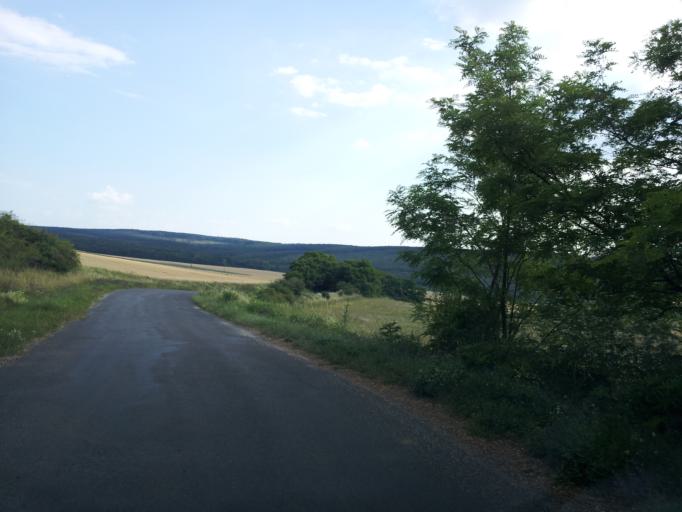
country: HU
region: Veszprem
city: Zanka
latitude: 46.9653
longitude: 17.6388
